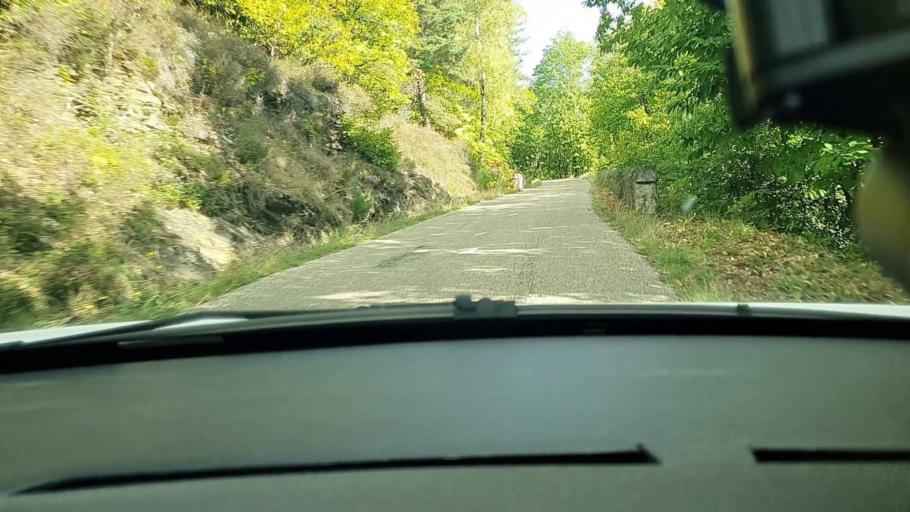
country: FR
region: Languedoc-Roussillon
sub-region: Departement du Gard
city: Besseges
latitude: 44.3761
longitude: 3.9911
